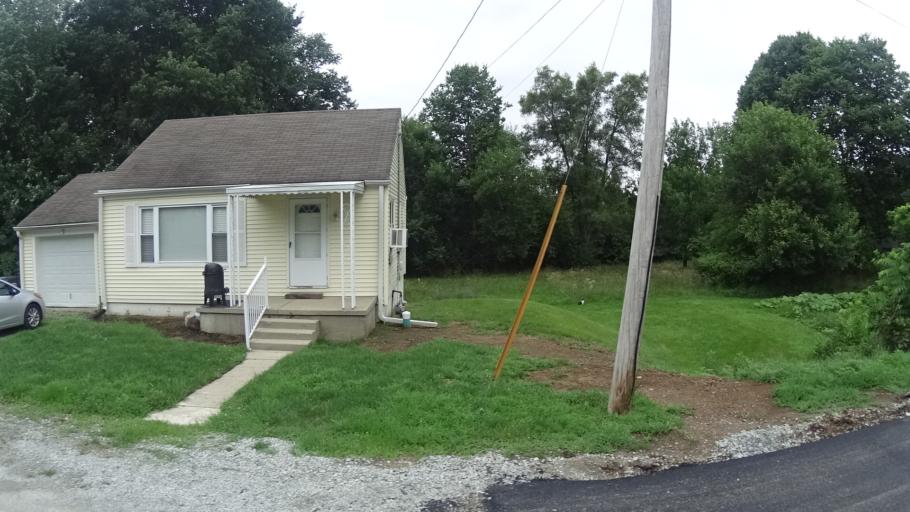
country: US
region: Indiana
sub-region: Madison County
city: Pendleton
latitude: 39.9987
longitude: -85.7531
